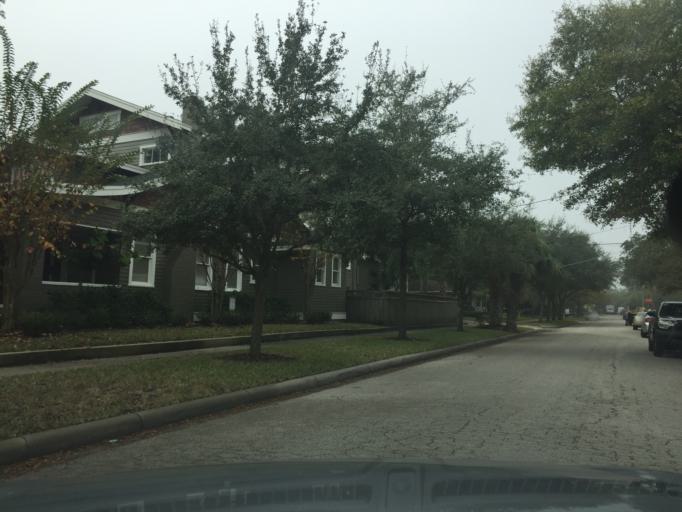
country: US
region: Florida
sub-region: Hillsborough County
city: Tampa
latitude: 27.9350
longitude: -82.4779
